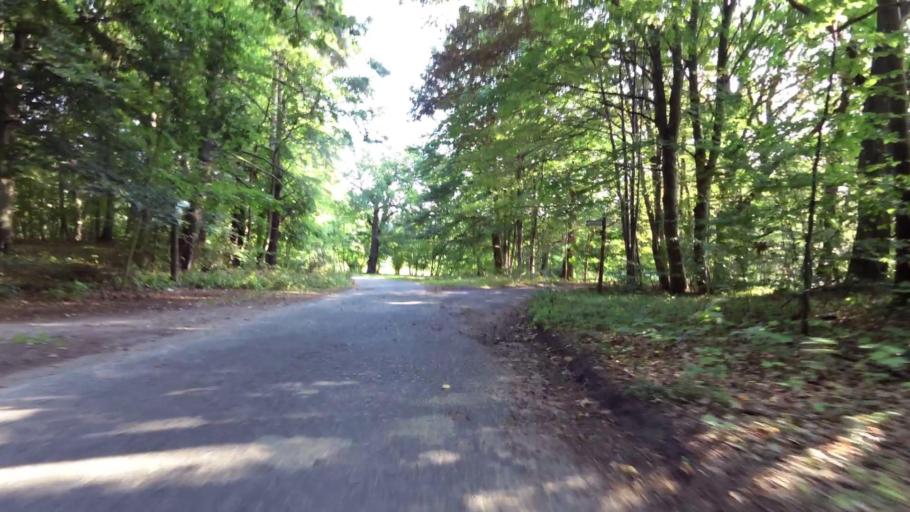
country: PL
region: West Pomeranian Voivodeship
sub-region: Powiat kamienski
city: Miedzyzdroje
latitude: 53.9316
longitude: 14.5366
